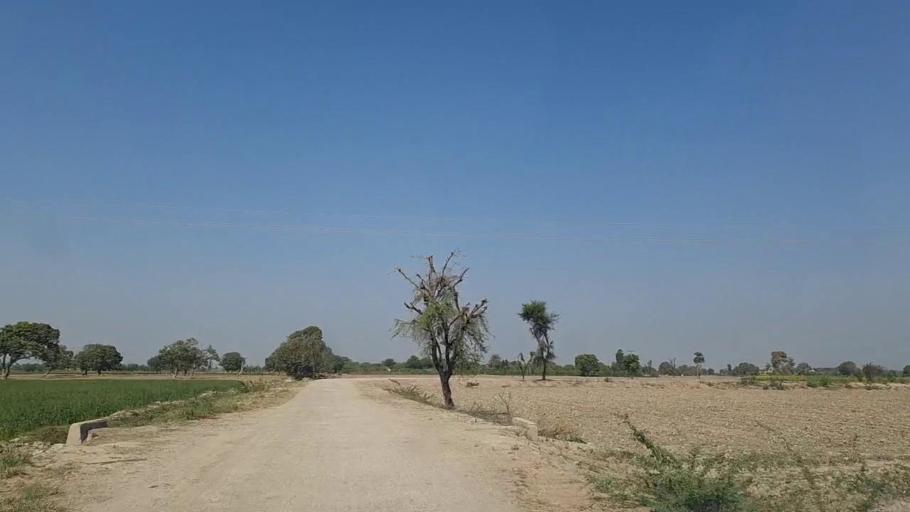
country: PK
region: Sindh
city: Naukot
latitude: 24.8563
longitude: 69.4156
